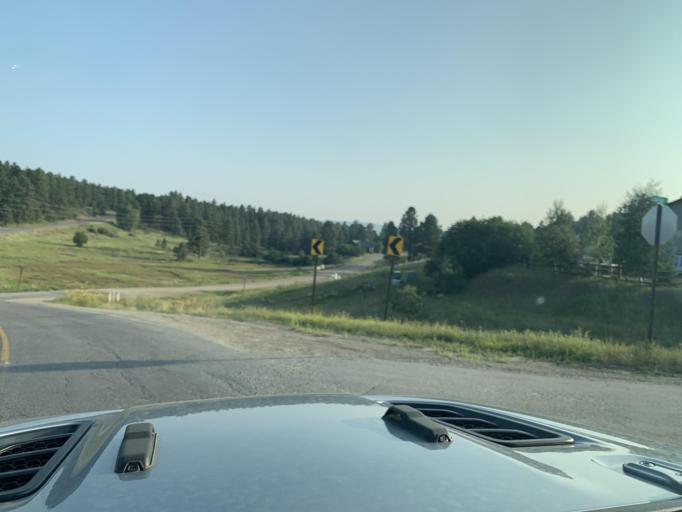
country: US
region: Colorado
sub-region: Archuleta County
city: Pagosa Springs
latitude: 37.2851
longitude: -107.0958
